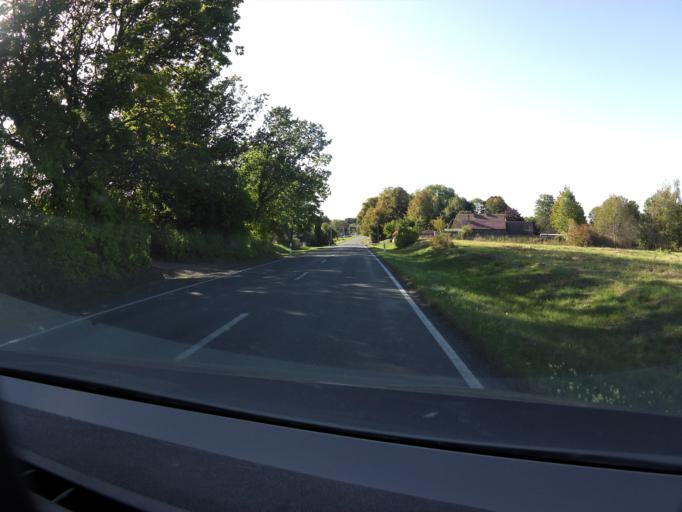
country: DE
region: Saxony-Anhalt
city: Hedersleben
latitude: 51.8774
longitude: 11.2228
